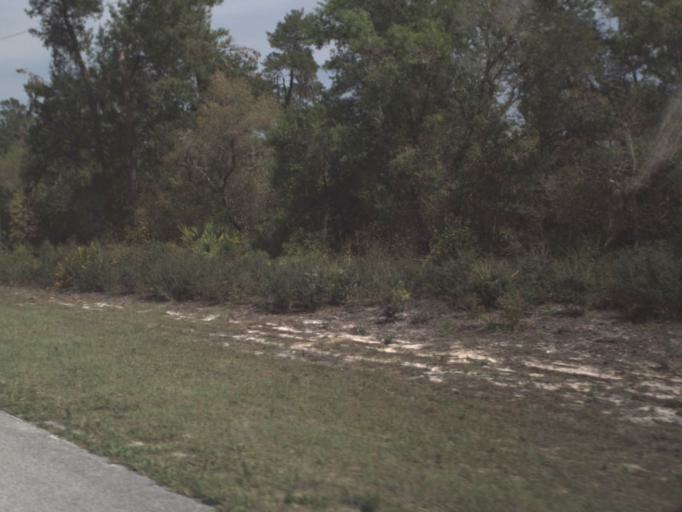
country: US
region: Florida
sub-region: Putnam County
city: Crescent City
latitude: 29.3129
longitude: -81.6901
